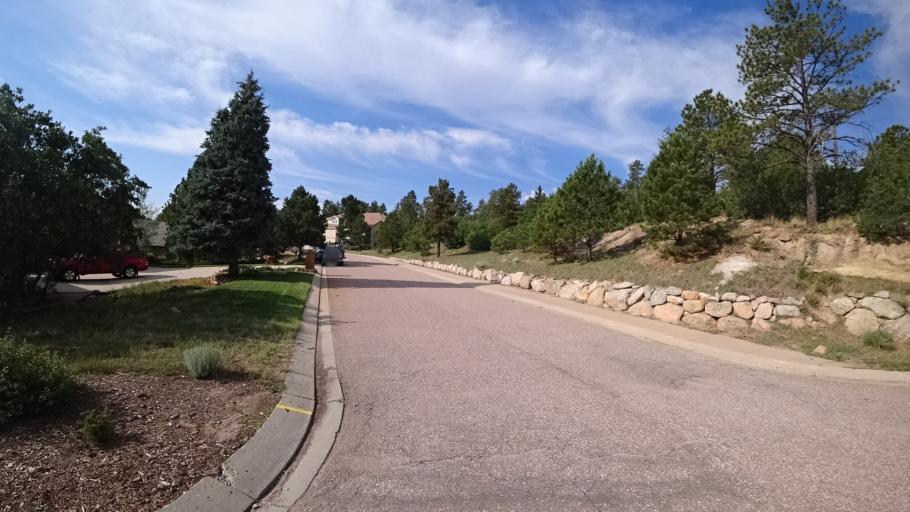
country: US
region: Colorado
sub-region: El Paso County
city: Air Force Academy
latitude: 38.9437
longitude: -104.8309
